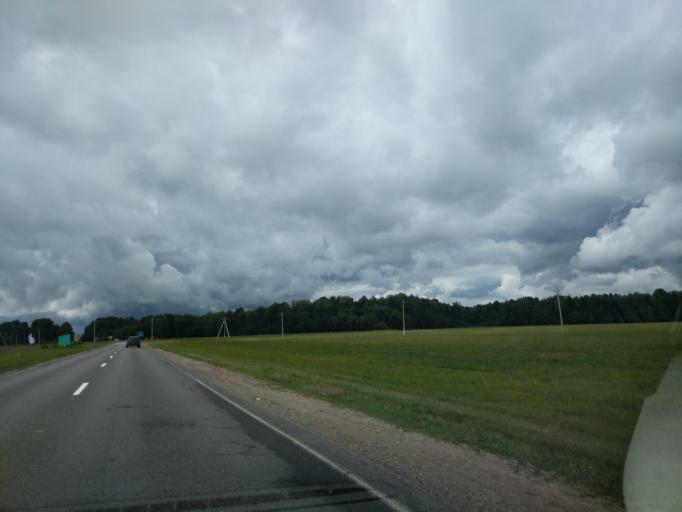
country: BY
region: Minsk
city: Il'ya
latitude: 54.4127
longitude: 27.2725
